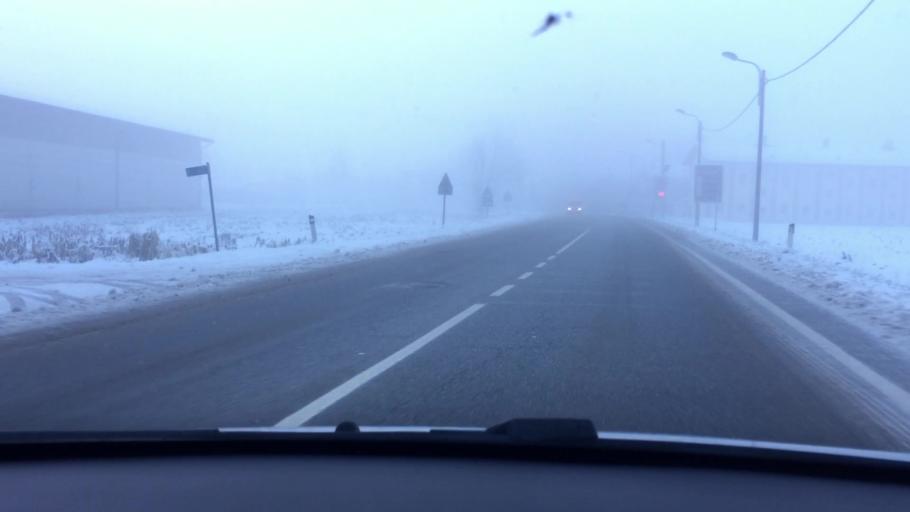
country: IT
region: Piedmont
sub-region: Provincia di Torino
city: Scalenghe
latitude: 44.8981
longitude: 7.4905
